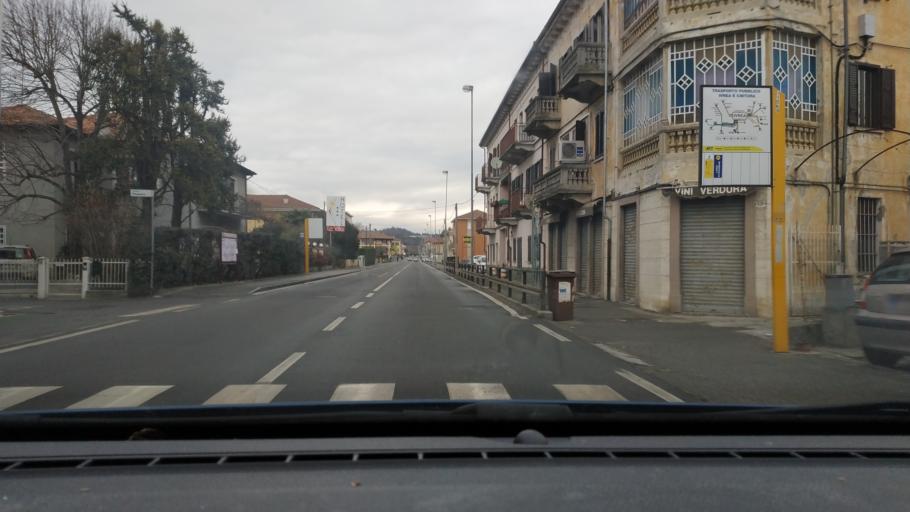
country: IT
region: Piedmont
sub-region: Provincia di Torino
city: Pavone Canavese
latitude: 45.4351
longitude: 7.8799
